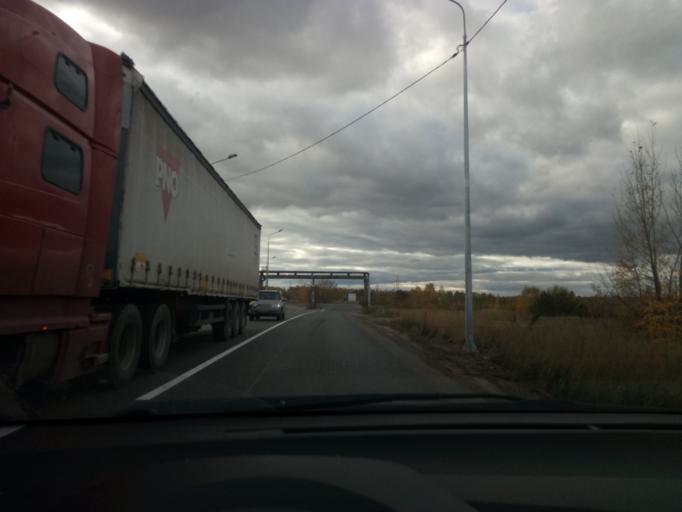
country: RU
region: Tatarstan
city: Staroye Arakchino
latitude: 55.8847
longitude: 48.9786
